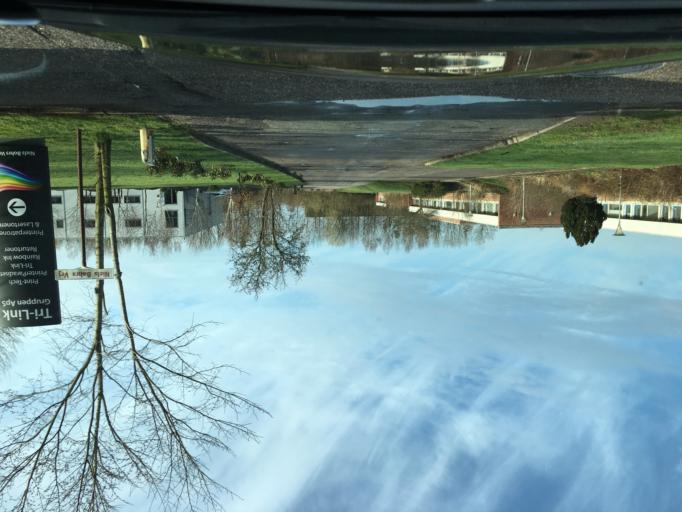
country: DK
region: South Denmark
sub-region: Kolding Kommune
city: Kolding
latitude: 55.5049
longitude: 9.4665
